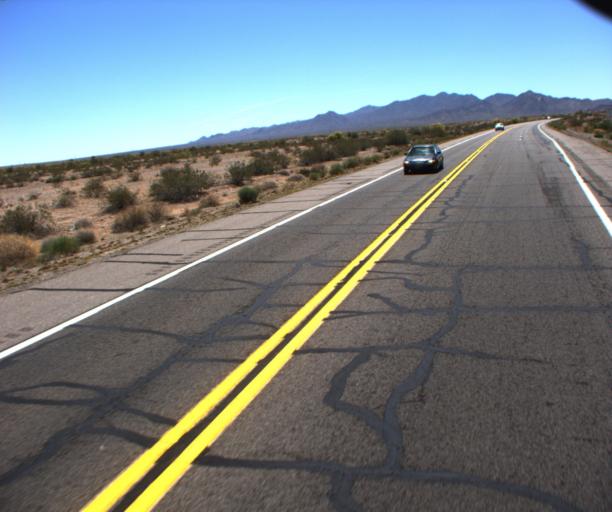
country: US
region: Arizona
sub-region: Mohave County
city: Desert Hills
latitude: 34.7062
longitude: -114.3038
